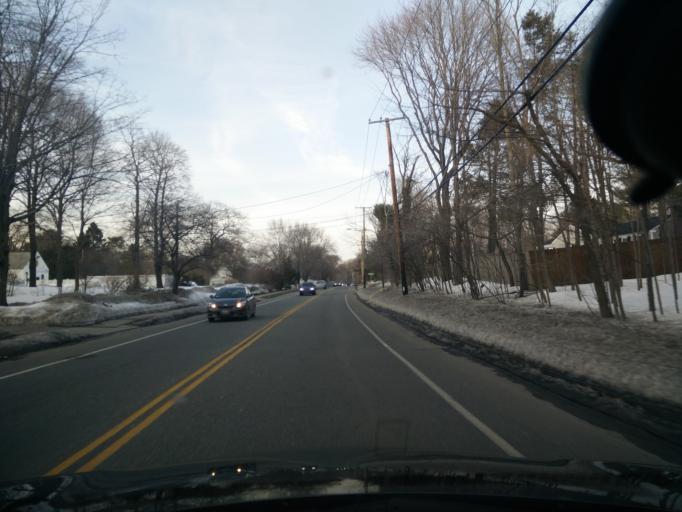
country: US
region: Massachusetts
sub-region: Norfolk County
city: Westwood
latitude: 42.2304
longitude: -71.2207
